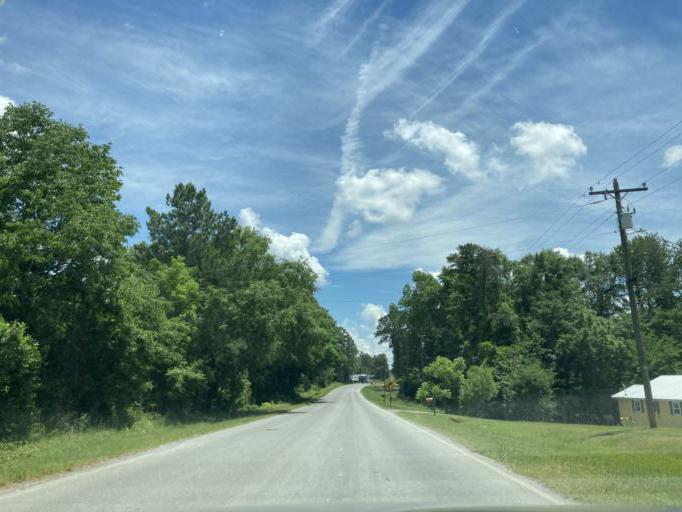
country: US
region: Georgia
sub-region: Jones County
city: Gray
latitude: 32.9078
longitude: -83.5247
